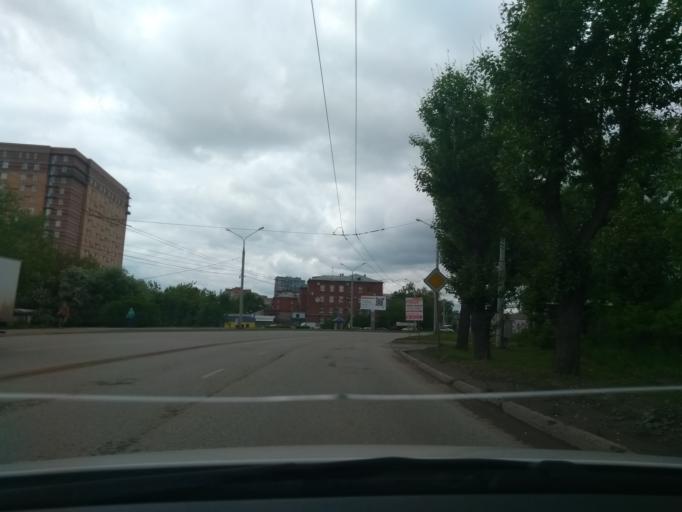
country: RU
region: Perm
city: Perm
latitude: 57.9829
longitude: 56.2470
